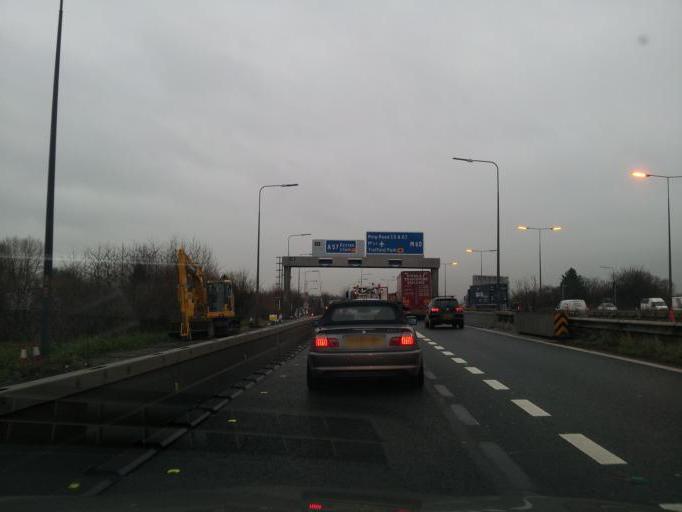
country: GB
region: England
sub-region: Manchester
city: Swinton
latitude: 53.4792
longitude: -2.3748
